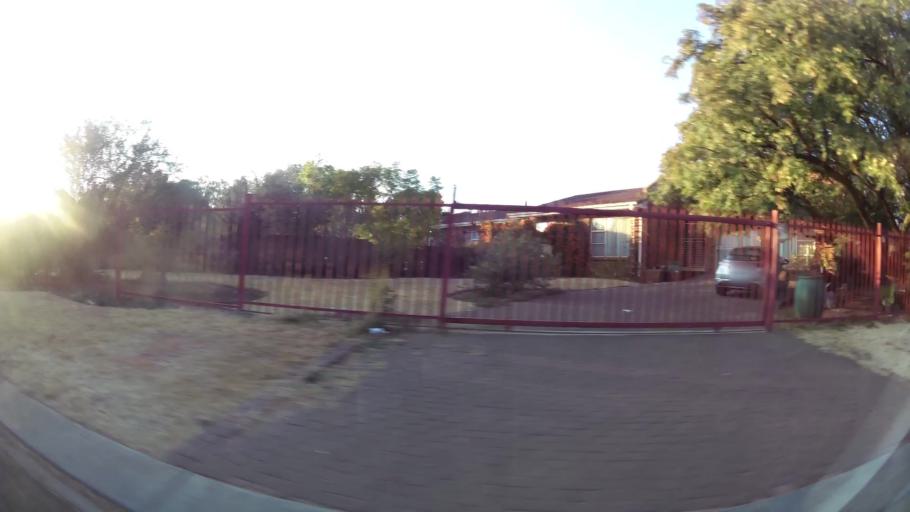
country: ZA
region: Orange Free State
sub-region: Mangaung Metropolitan Municipality
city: Bloemfontein
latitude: -29.0904
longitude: 26.1542
